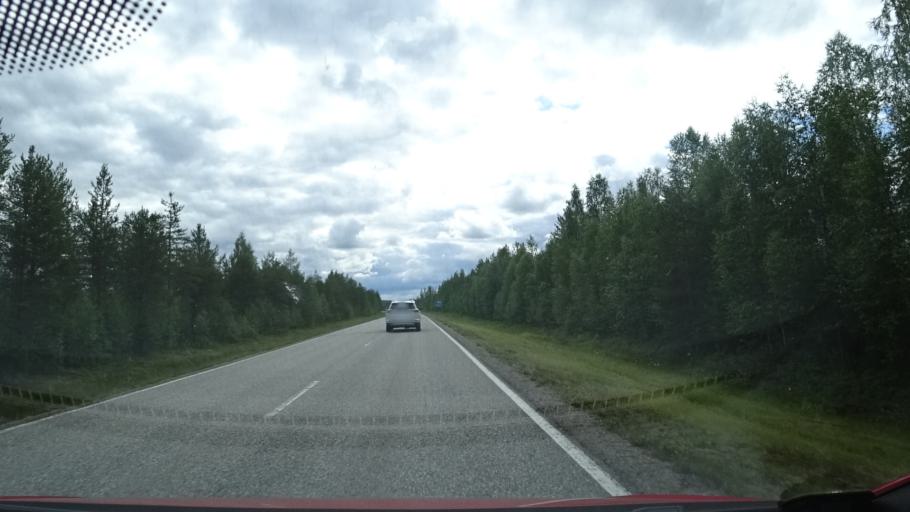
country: FI
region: Lapland
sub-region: Tunturi-Lappi
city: Kittilae
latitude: 67.4578
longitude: 24.9471
